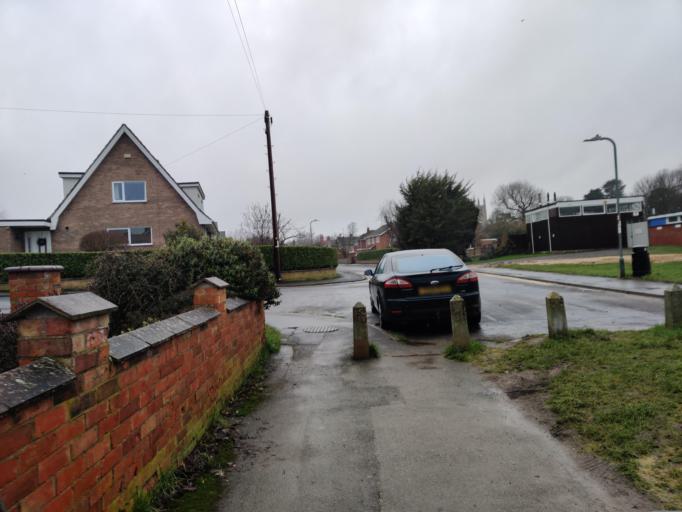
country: GB
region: England
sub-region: Lincolnshire
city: Bourne
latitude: 52.7654
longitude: -0.3720
